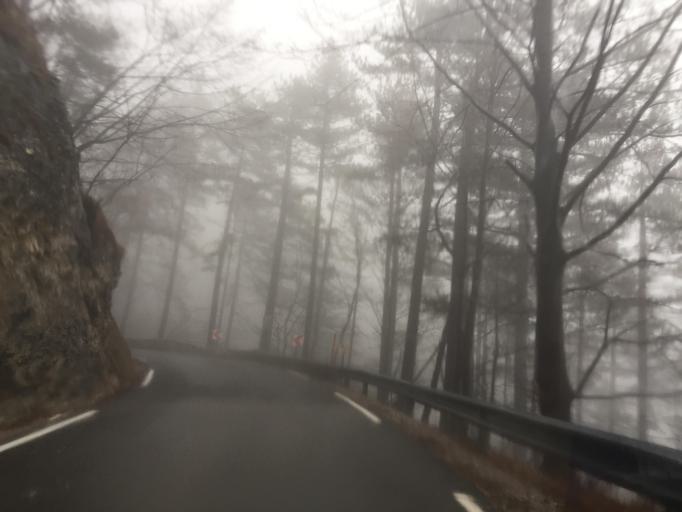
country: SI
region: Ajdovscina
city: Lokavec
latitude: 45.9385
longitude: 13.8692
